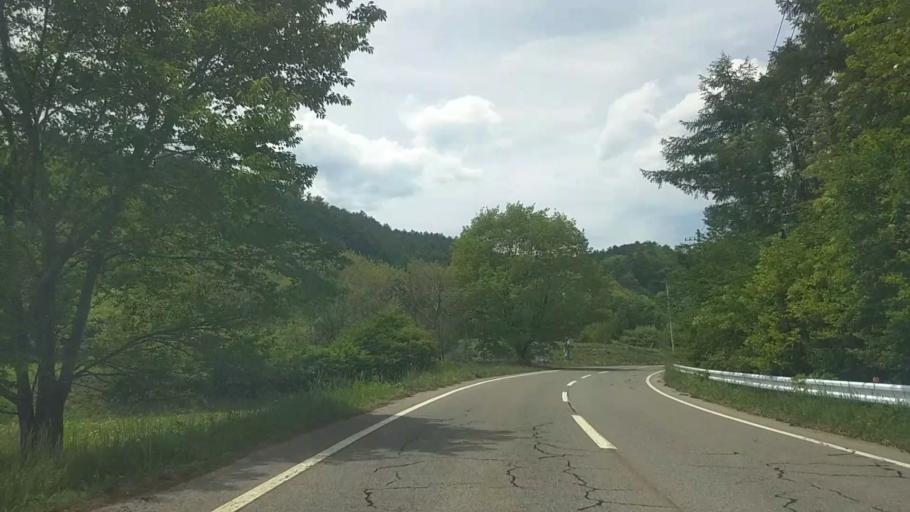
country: JP
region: Nagano
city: Saku
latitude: 36.1053
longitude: 138.4271
